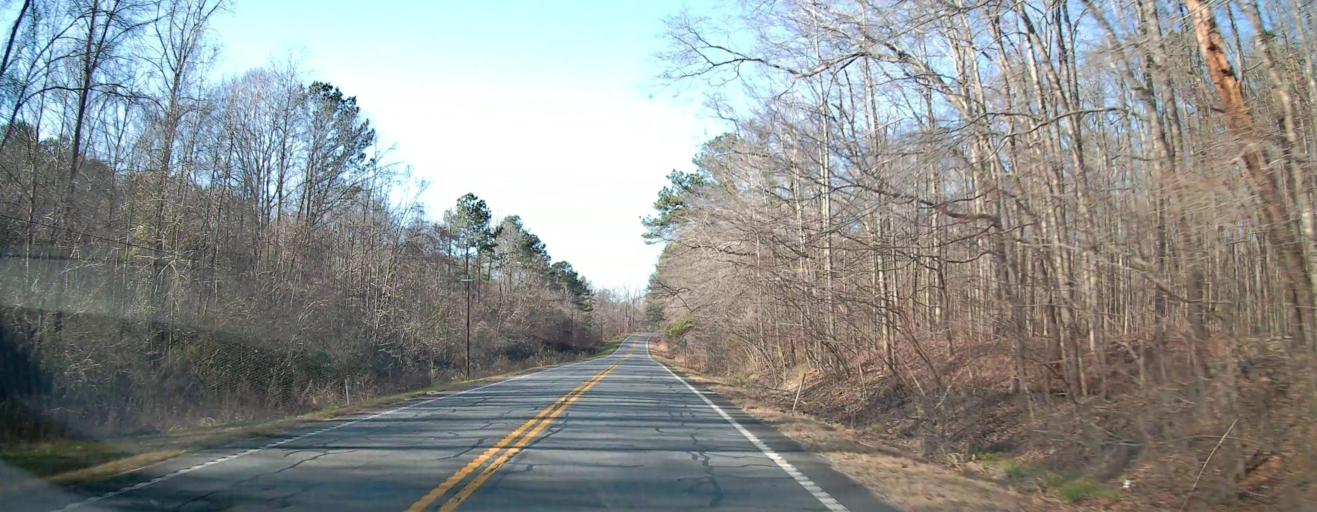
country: US
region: Georgia
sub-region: Talbot County
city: Talbotton
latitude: 32.6986
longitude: -84.5502
